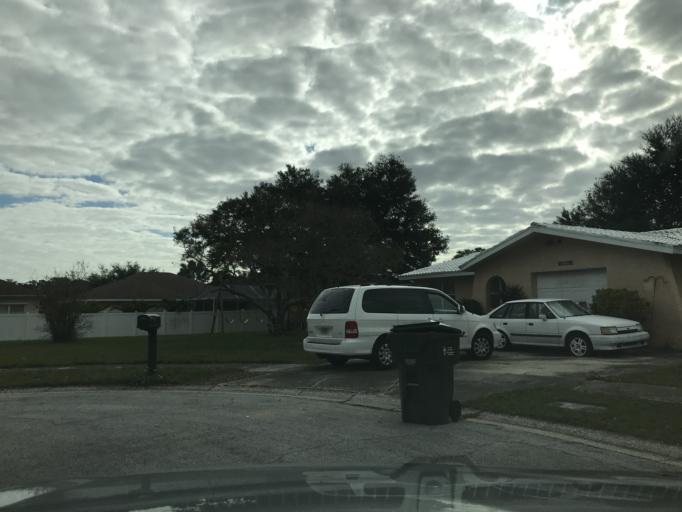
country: US
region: Florida
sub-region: Pinellas County
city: Largo
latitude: 27.9289
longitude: -82.7795
